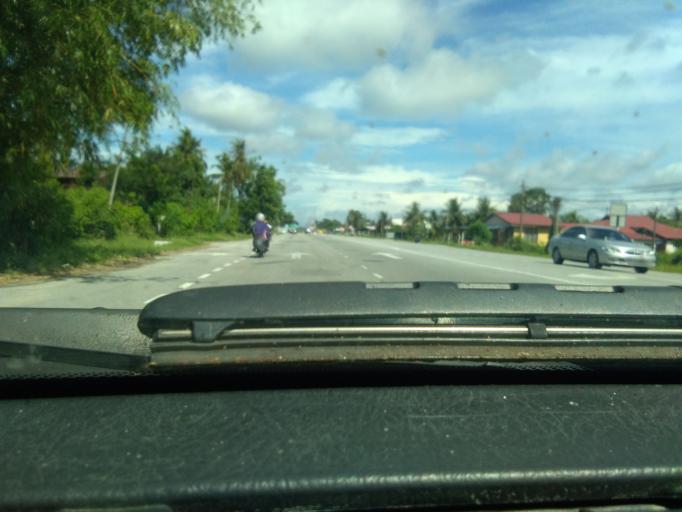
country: MY
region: Perak
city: Bagan Serai
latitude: 5.0035
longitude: 100.5479
